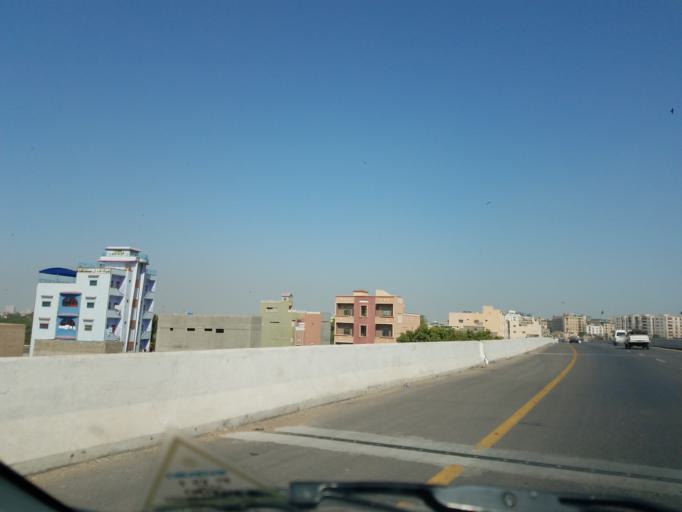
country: PK
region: Sindh
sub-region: Karachi District
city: Karachi
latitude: 24.8794
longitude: 67.0110
